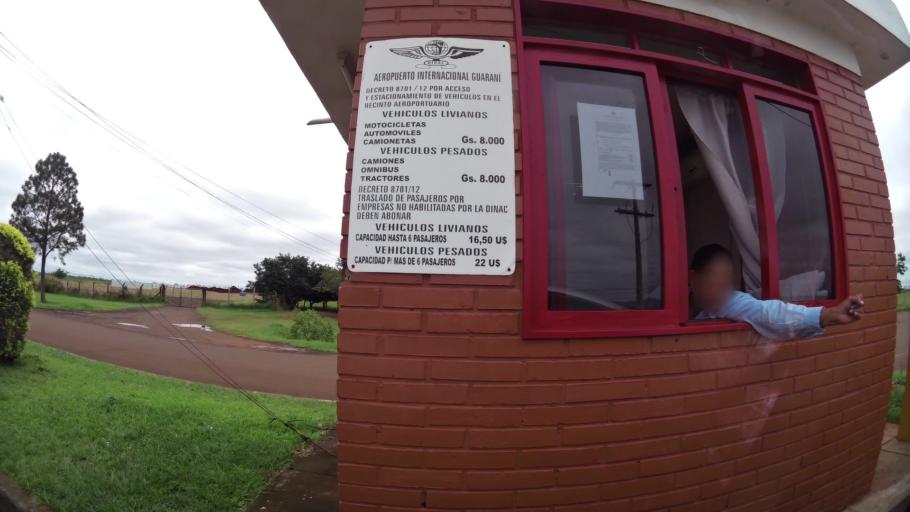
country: PY
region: Alto Parana
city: Colonia Yguazu
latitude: -25.4605
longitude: -54.8407
